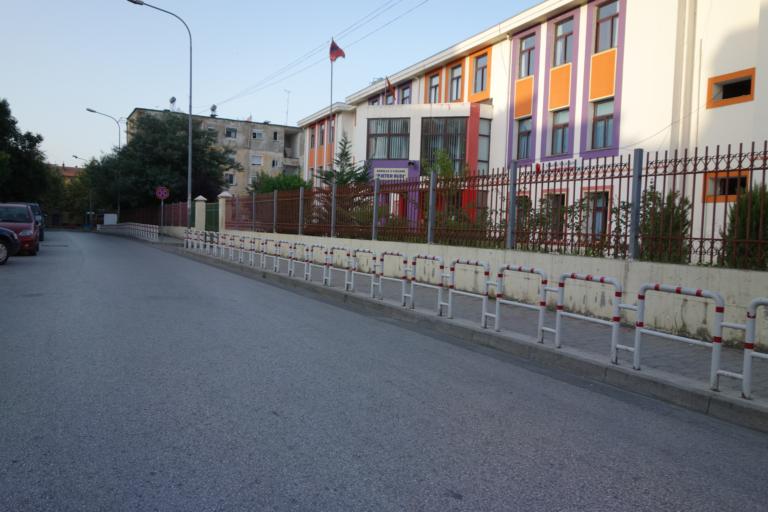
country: AL
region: Tirane
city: Tirana
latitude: 41.3230
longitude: 19.8070
